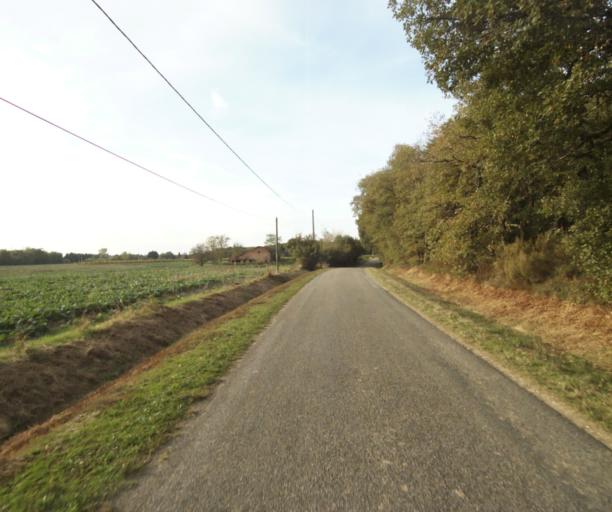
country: FR
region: Midi-Pyrenees
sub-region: Departement du Tarn-et-Garonne
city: Campsas
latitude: 43.8757
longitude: 1.3256
